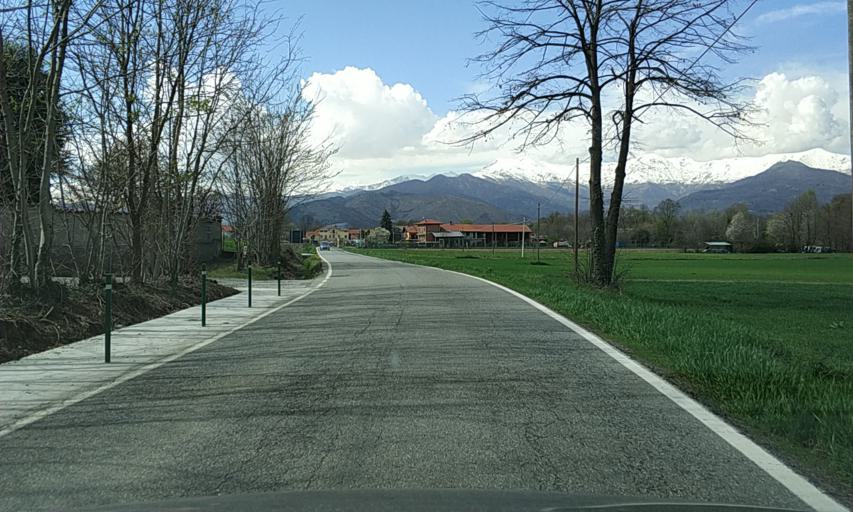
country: IT
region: Piedmont
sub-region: Provincia di Torino
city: San Carlo Canavese
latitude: 45.2545
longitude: 7.5873
